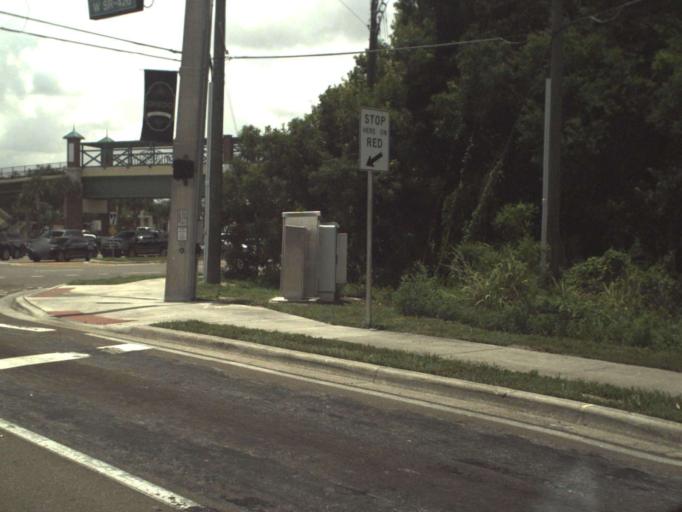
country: US
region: Florida
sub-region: Seminole County
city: Oviedo
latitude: 28.6559
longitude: -81.2258
